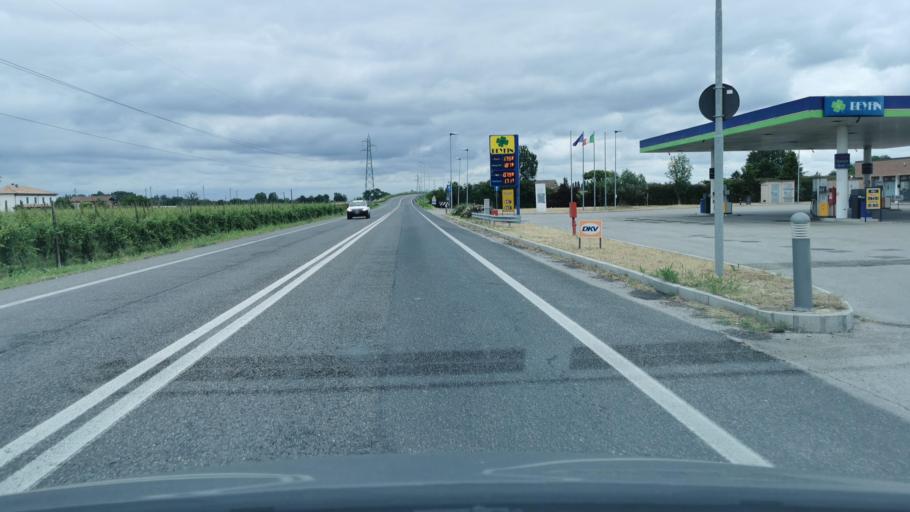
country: IT
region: Emilia-Romagna
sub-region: Provincia di Ravenna
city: Granarolo
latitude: 44.3650
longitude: 11.9359
